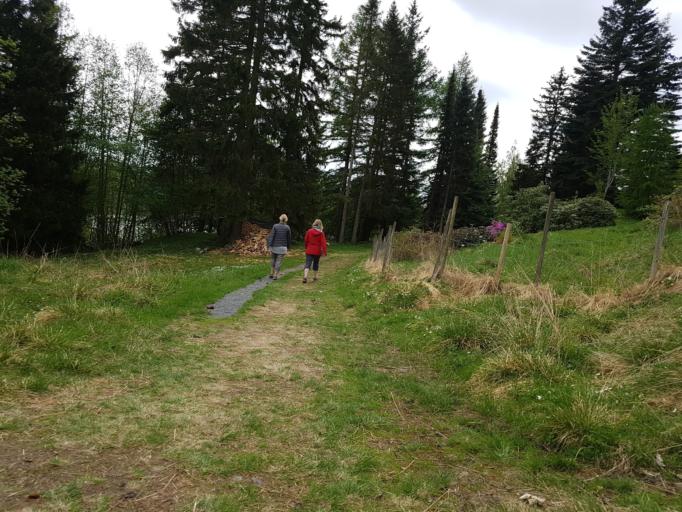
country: NO
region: Nord-Trondelag
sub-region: Levanger
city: Levanger
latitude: 63.7430
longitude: 11.2708
